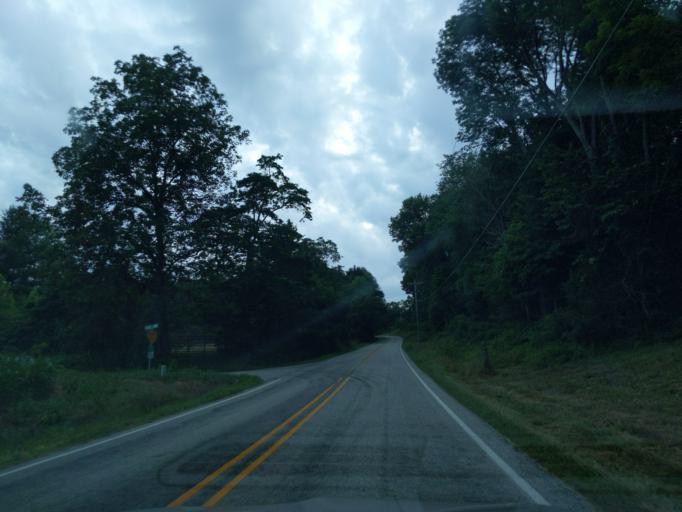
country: US
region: Indiana
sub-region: Ripley County
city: Osgood
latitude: 39.1950
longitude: -85.2573
